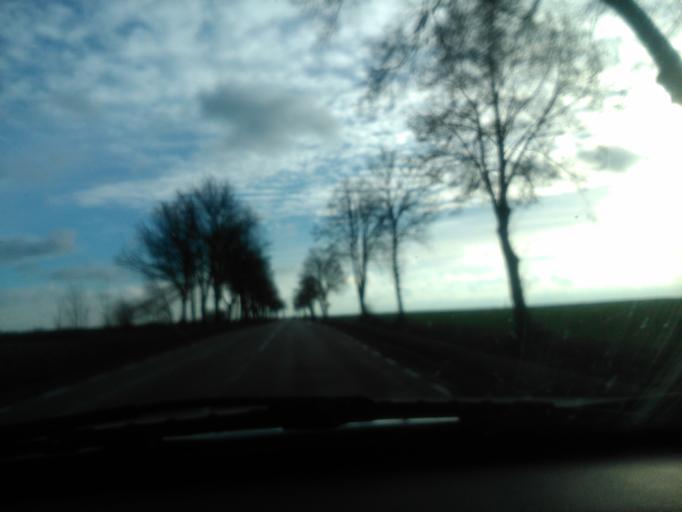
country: PL
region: Podlasie
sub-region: Powiat kolnenski
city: Kolno
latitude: 53.4192
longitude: 21.8961
